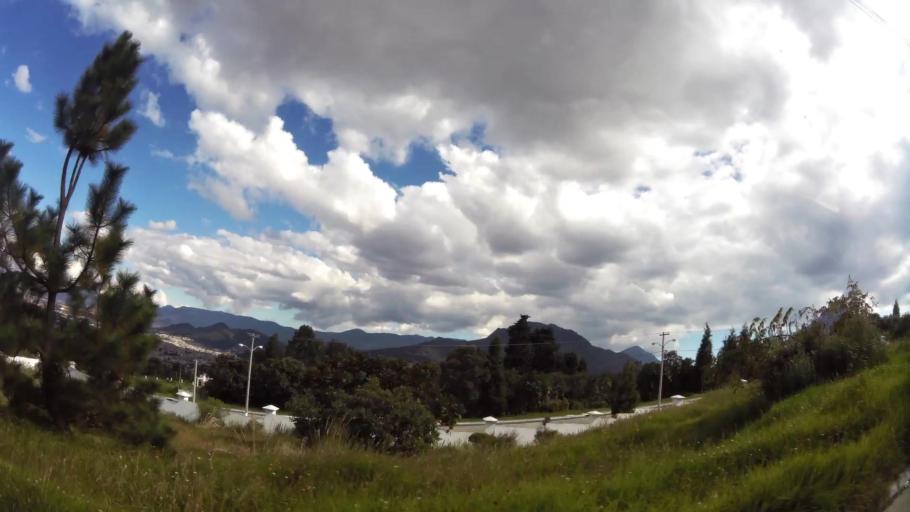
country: GT
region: Quetzaltenango
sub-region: Municipio de La Esperanza
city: La Esperanza
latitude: 14.8349
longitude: -91.5584
